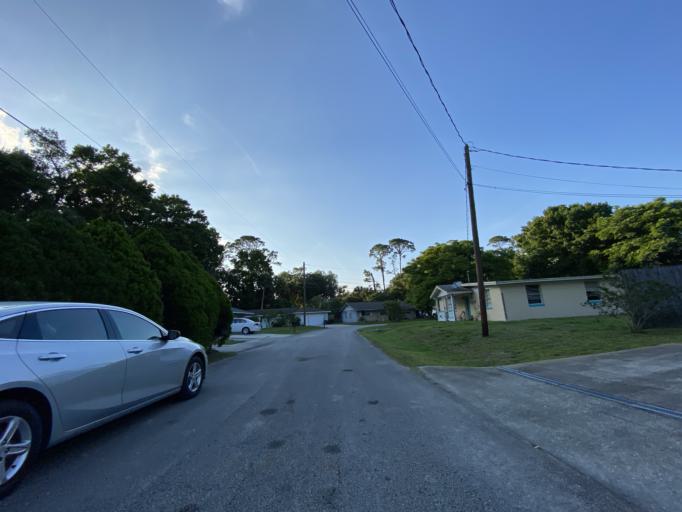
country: US
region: Florida
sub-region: Volusia County
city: Port Orange
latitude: 29.1459
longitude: -81.0043
